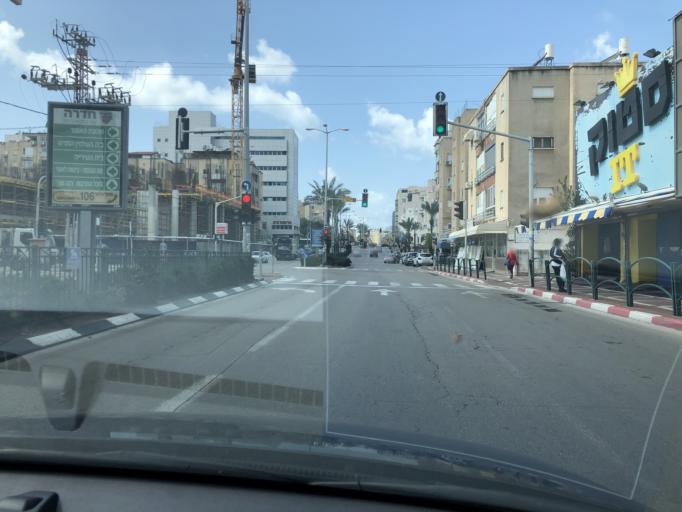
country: IL
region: Haifa
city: Hadera
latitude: 32.4406
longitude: 34.9168
